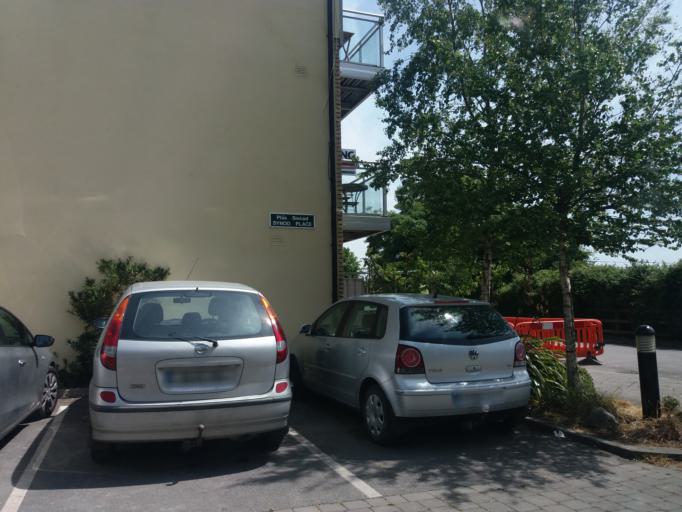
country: IE
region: Leinster
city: Lusk
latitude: 53.5261
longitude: -6.1599
